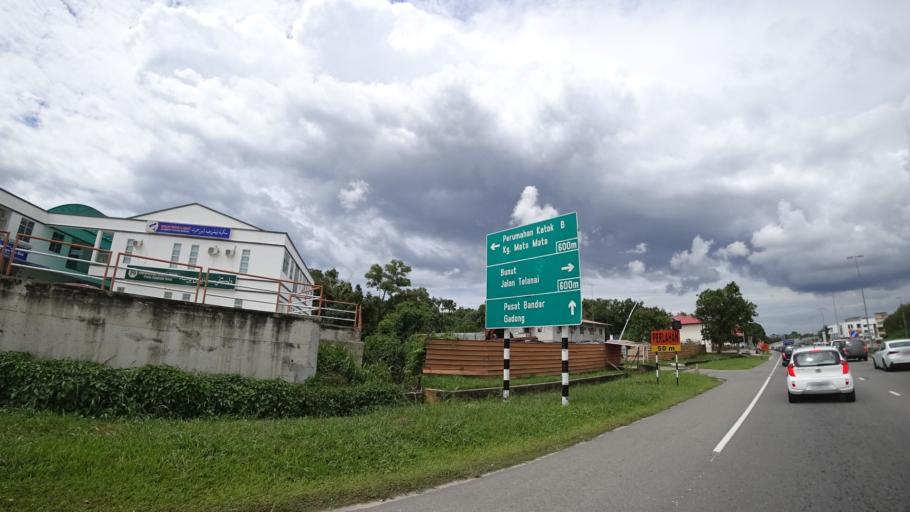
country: BN
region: Brunei and Muara
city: Bandar Seri Begawan
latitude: 4.8805
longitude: 114.8878
